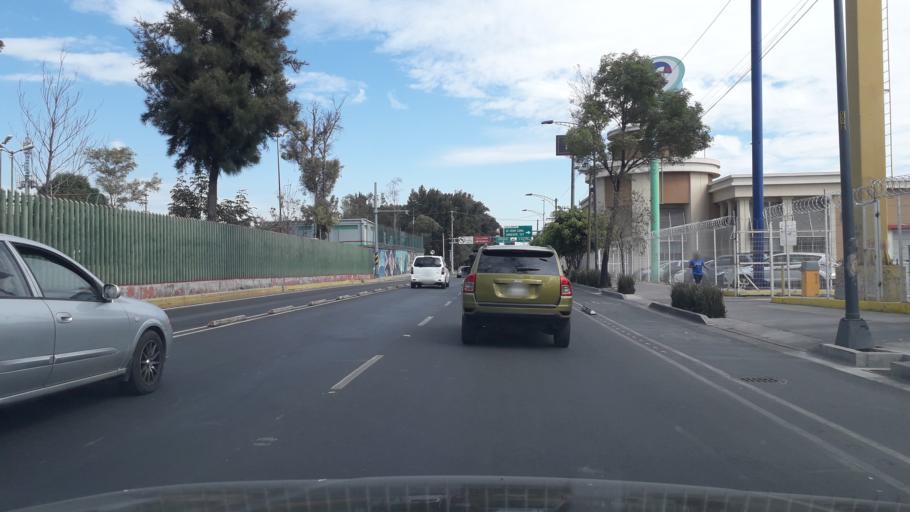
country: MX
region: Mexico City
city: Gustavo A. Madero
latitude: 19.4860
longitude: -99.0946
